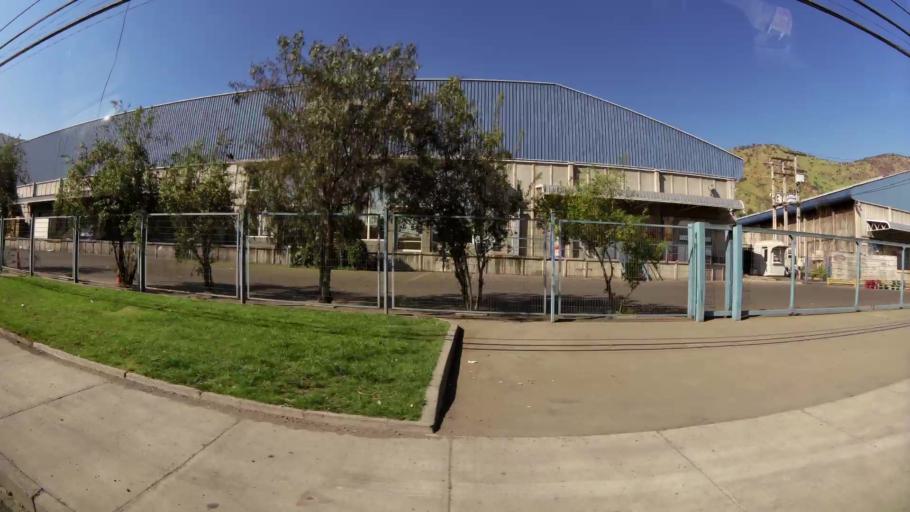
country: CL
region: Santiago Metropolitan
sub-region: Provincia de Chacabuco
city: Chicureo Abajo
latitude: -33.3372
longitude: -70.6957
